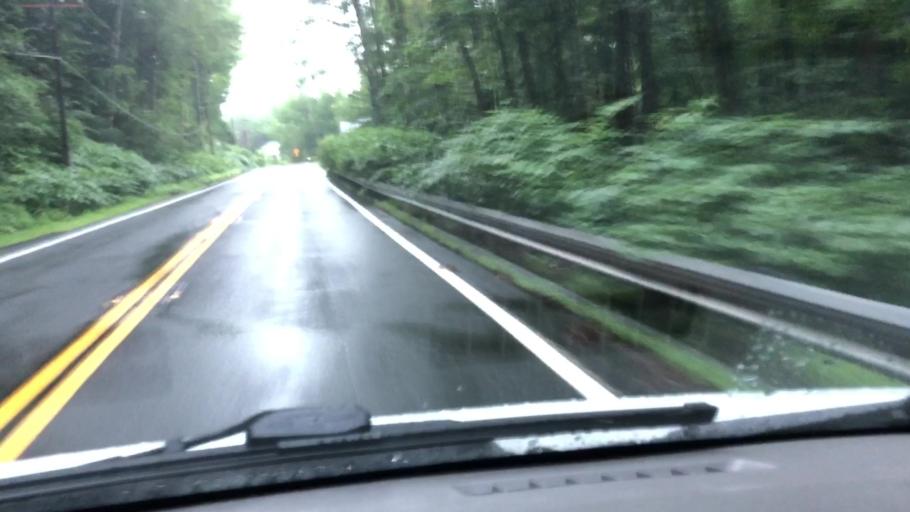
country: US
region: Massachusetts
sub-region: Hampshire County
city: Chesterfield
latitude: 42.3414
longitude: -72.8880
